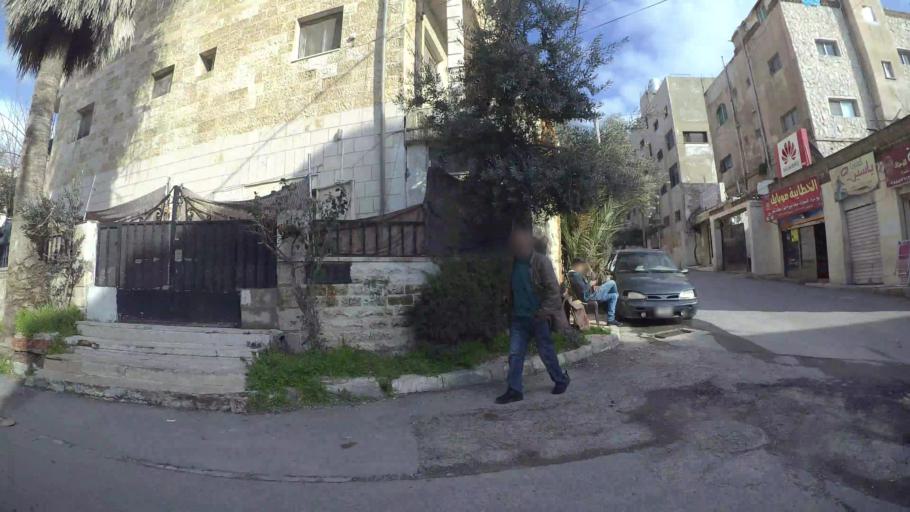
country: JO
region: Amman
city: Al Jubayhah
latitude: 32.0205
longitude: 35.8460
